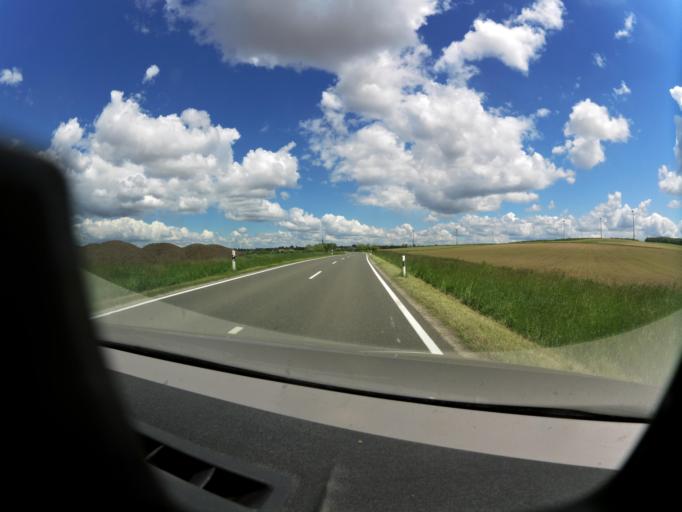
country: DE
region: Bavaria
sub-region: Regierungsbezirk Unterfranken
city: Prosselsheim
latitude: 49.8868
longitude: 10.1200
